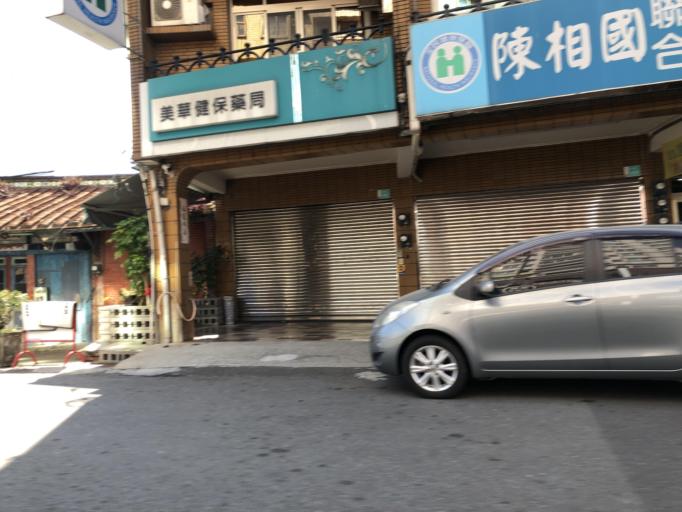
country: TW
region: Taiwan
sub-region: Tainan
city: Tainan
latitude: 23.0359
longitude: 120.3028
